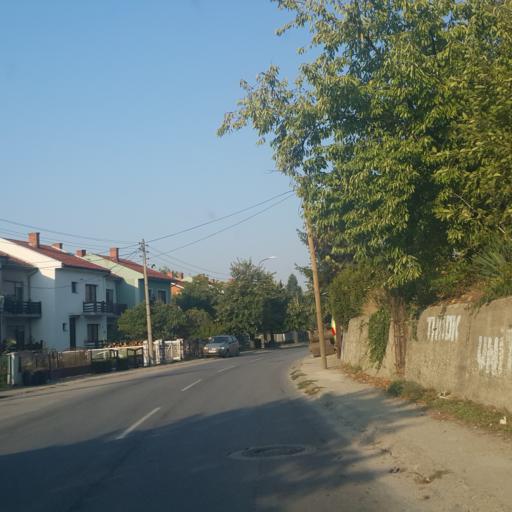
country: RS
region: Central Serbia
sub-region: Zajecarski Okrug
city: Zajecar
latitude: 43.9139
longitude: 22.2780
